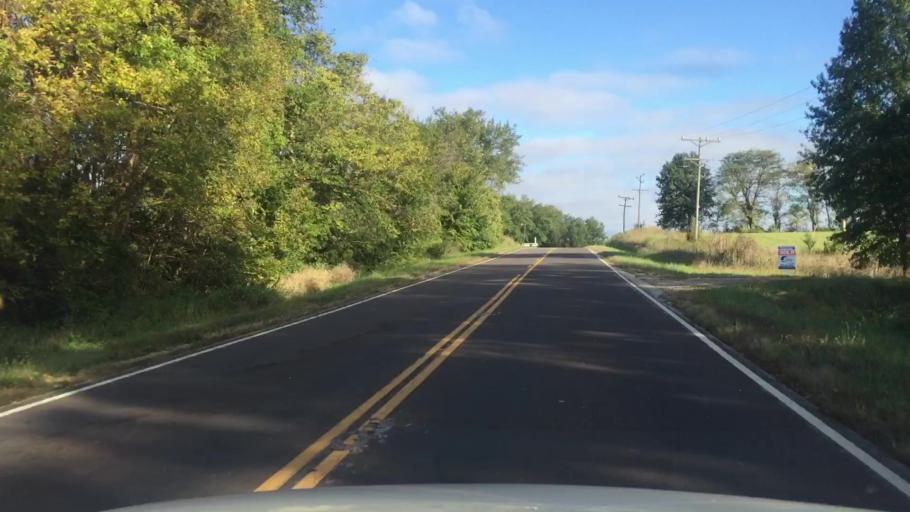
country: US
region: Missouri
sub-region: Howard County
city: New Franklin
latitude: 39.0375
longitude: -92.7440
